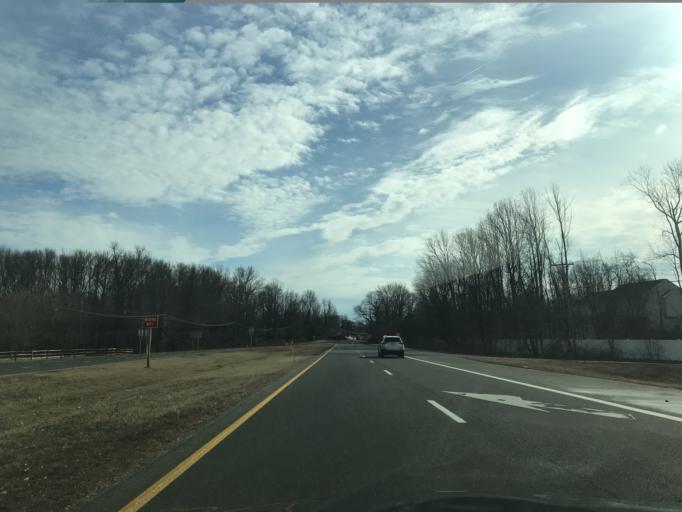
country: US
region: Maryland
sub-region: Prince George's County
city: Glenn Dale
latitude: 38.9609
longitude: -76.7977
